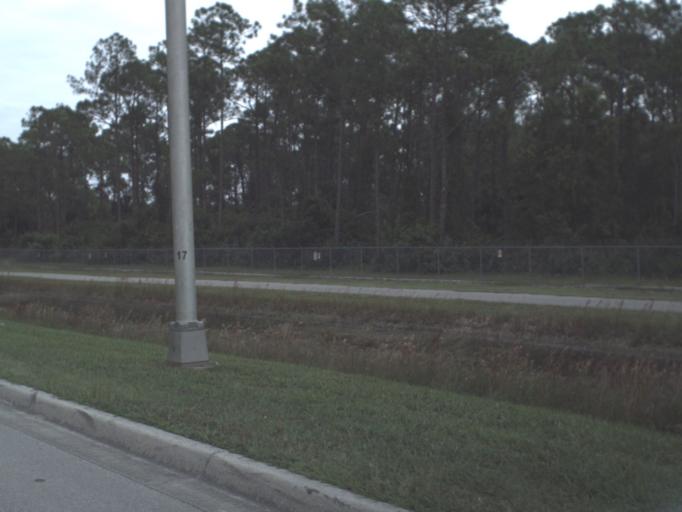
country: US
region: Florida
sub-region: Collier County
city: Lely Resort
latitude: 26.0709
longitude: -81.6932
